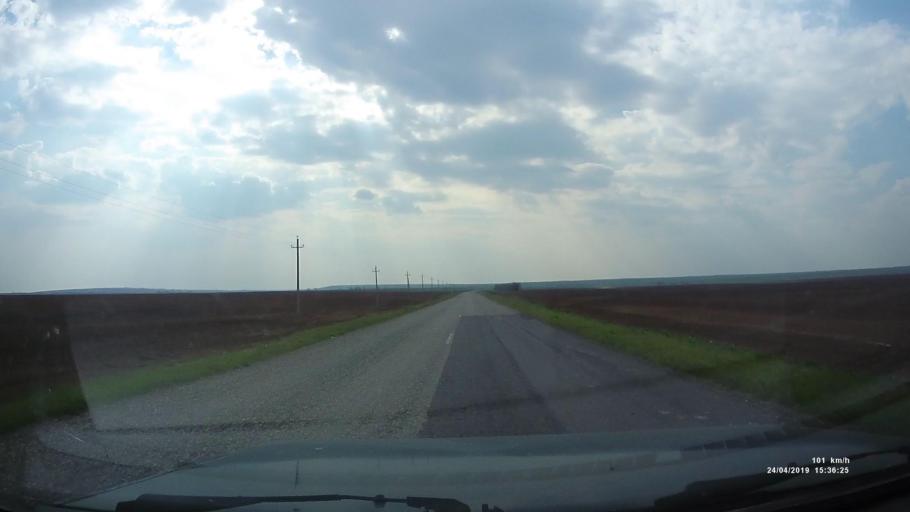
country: RU
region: Kalmykiya
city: Yashalta
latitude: 46.5992
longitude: 42.8709
